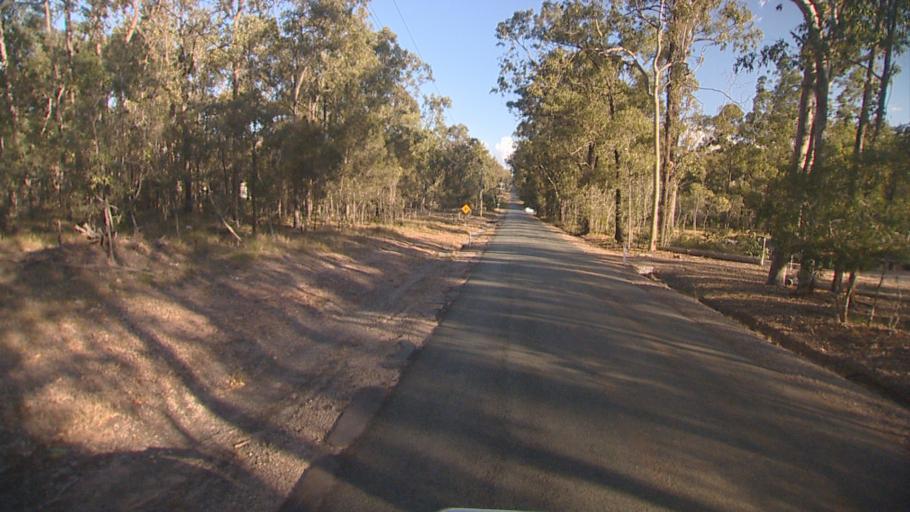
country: AU
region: Queensland
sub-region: Ipswich
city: Springfield Lakes
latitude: -27.7038
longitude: 152.9478
